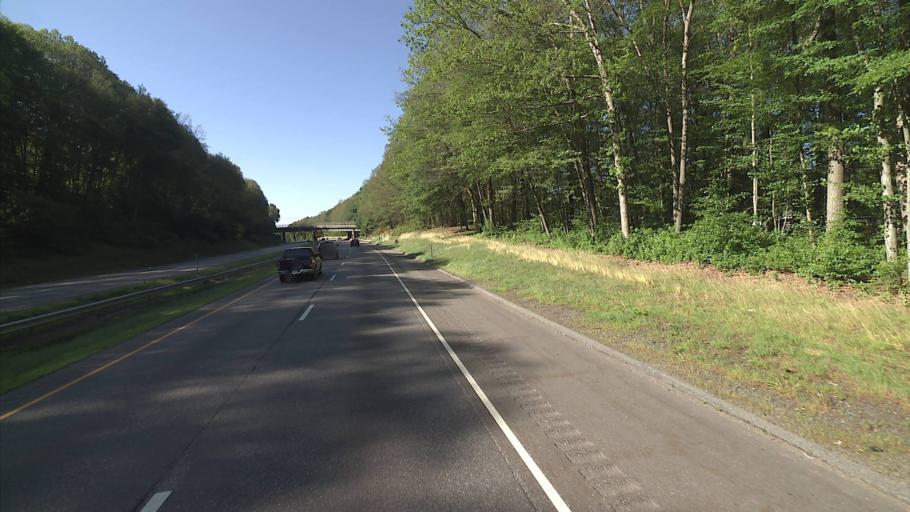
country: US
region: Connecticut
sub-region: New London County
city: Norwich
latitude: 41.5196
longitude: -72.1195
